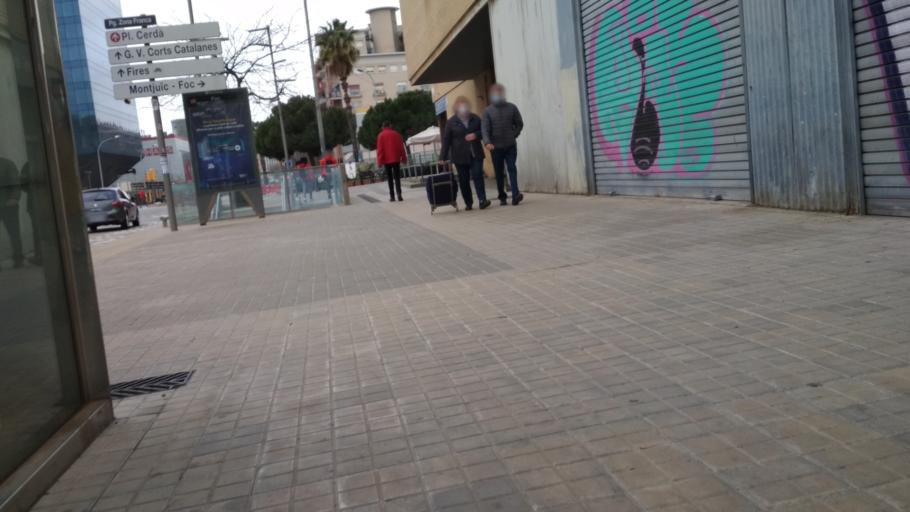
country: ES
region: Catalonia
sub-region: Provincia de Barcelona
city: Sants-Montjuic
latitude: 41.3559
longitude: 2.1424
